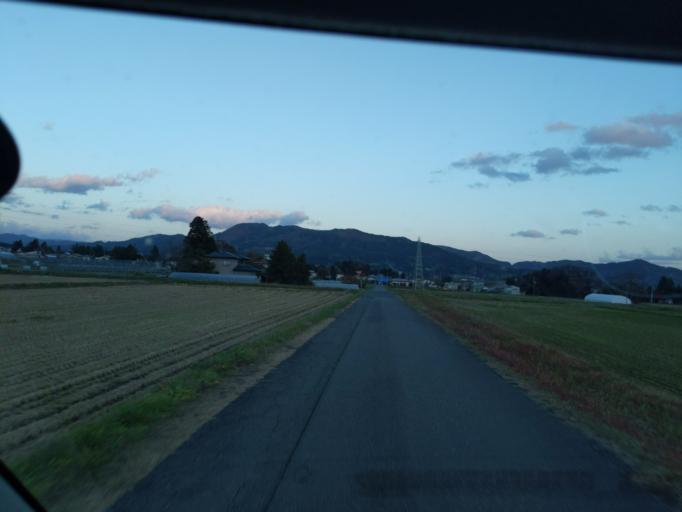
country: JP
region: Iwate
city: Ichinoseki
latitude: 39.0119
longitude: 141.1040
